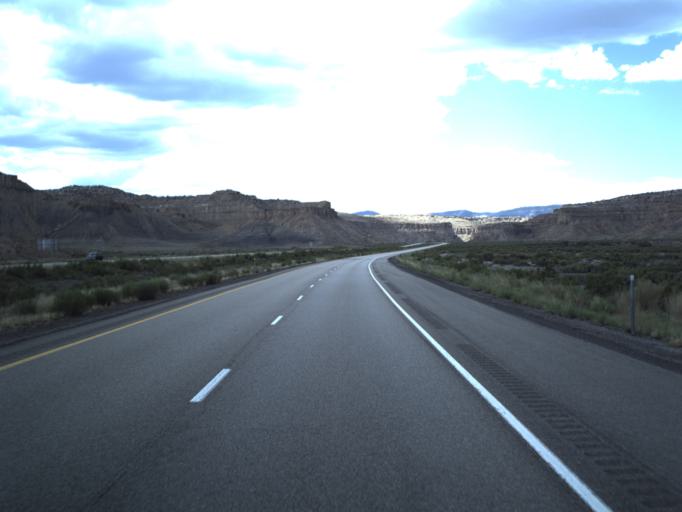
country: US
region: Utah
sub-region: Emery County
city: Ferron
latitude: 38.8100
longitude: -111.2266
